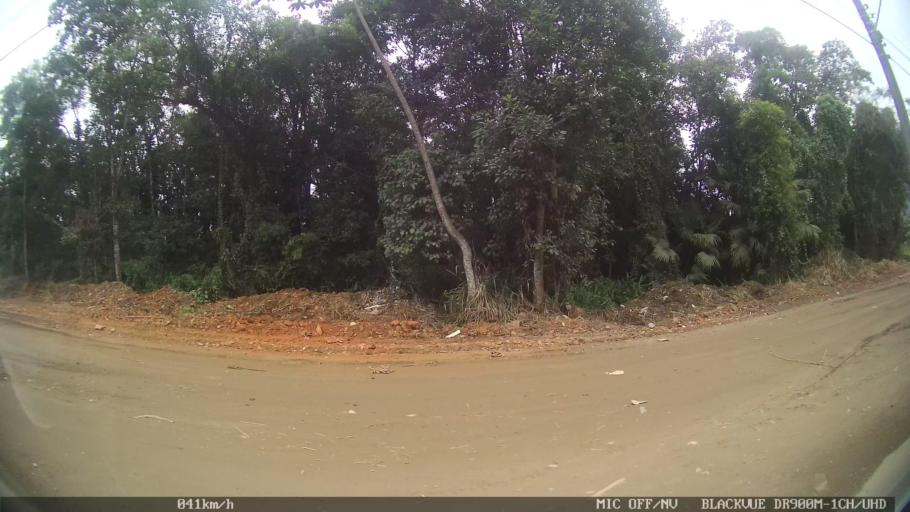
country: BR
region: Santa Catarina
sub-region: Joinville
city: Joinville
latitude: -26.2394
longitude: -48.8924
